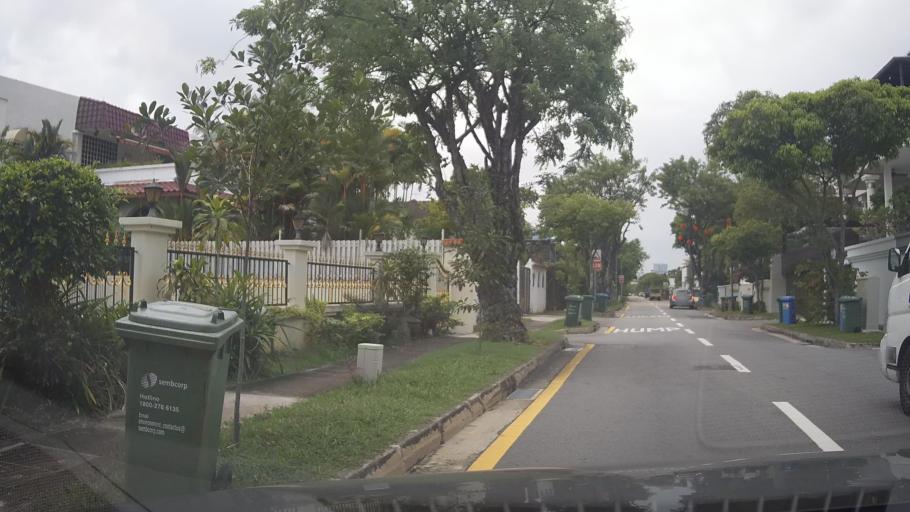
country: SG
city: Singapore
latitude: 1.3039
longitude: 103.8940
